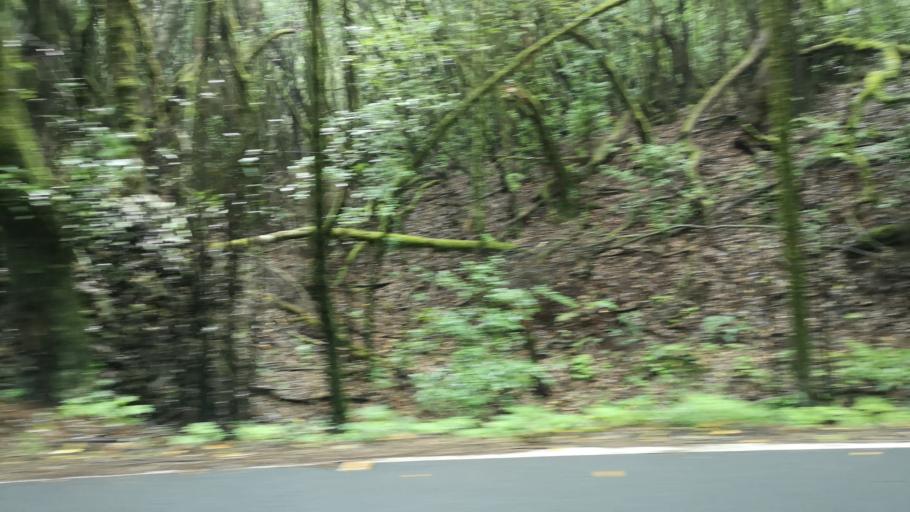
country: ES
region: Canary Islands
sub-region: Provincia de Santa Cruz de Tenerife
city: Vallehermosa
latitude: 28.1521
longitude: -17.3002
